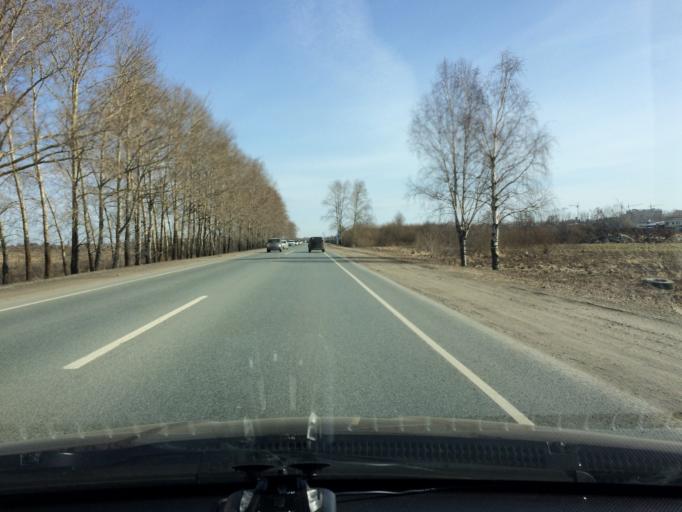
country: RU
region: Mariy-El
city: Yoshkar-Ola
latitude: 56.6513
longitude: 47.9486
